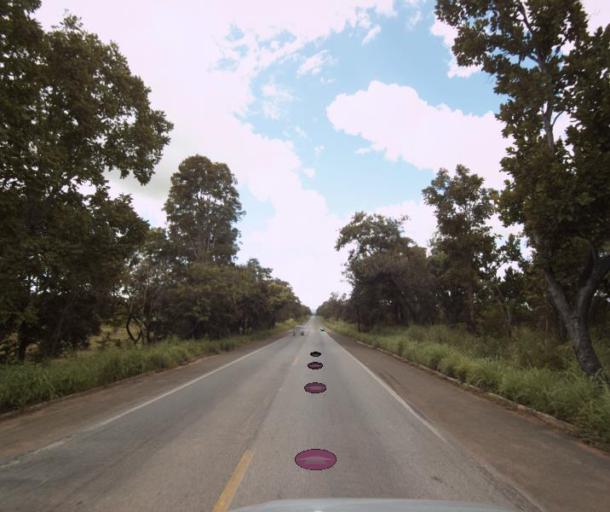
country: BR
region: Goias
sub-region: Porangatu
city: Porangatu
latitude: -13.7889
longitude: -49.0343
